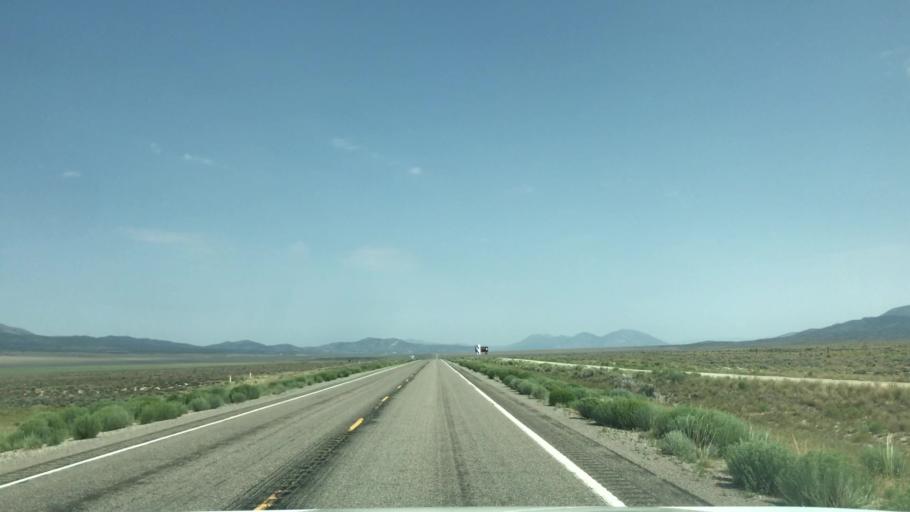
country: US
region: Nevada
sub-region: White Pine County
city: Ely
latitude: 39.0852
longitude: -114.7494
